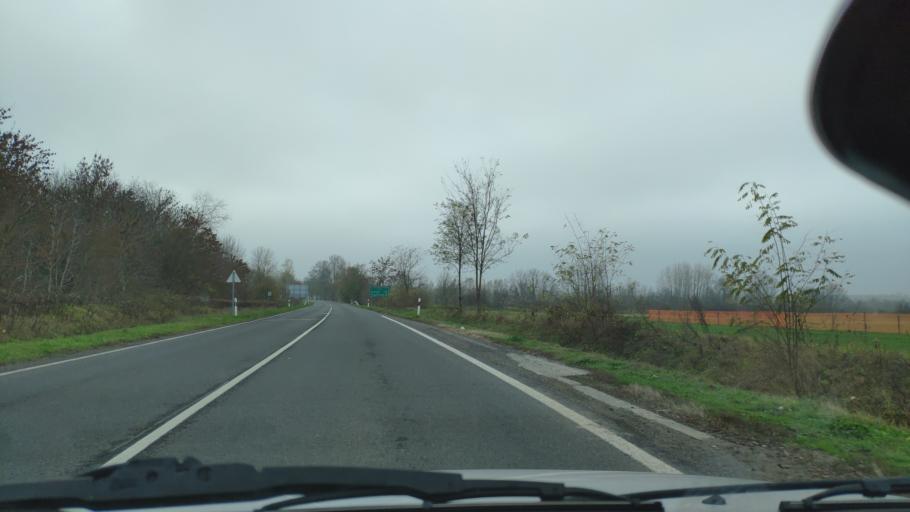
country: HU
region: Somogy
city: Balatonbereny
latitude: 46.6413
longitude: 17.2994
